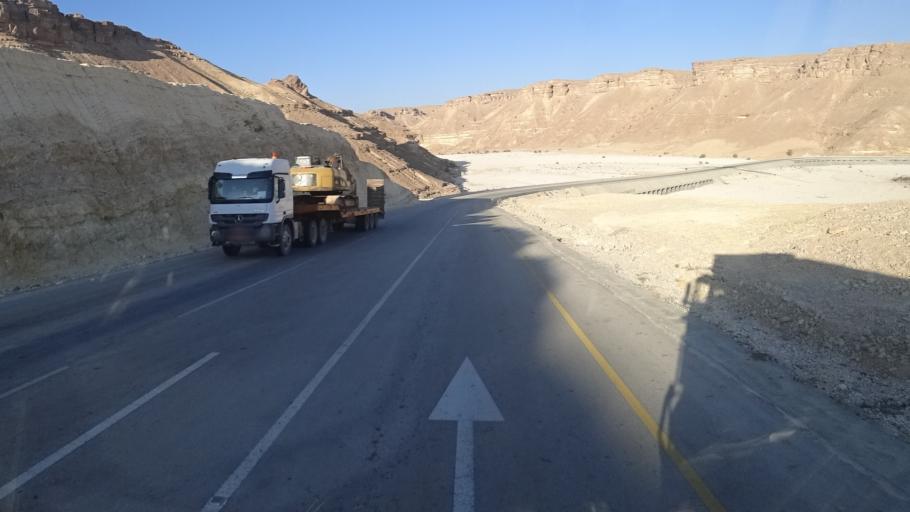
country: YE
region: Al Mahrah
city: Hawf
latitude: 17.0968
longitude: 53.0469
